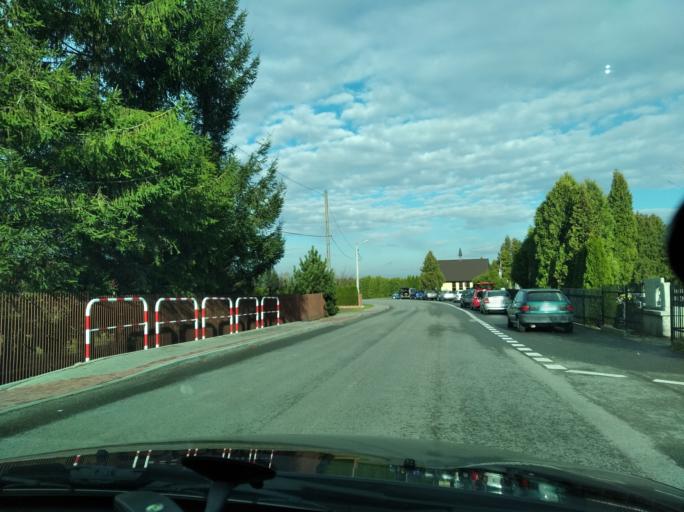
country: PL
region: Subcarpathian Voivodeship
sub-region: Powiat debicki
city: Brzeznica
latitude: 50.0630
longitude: 21.5284
